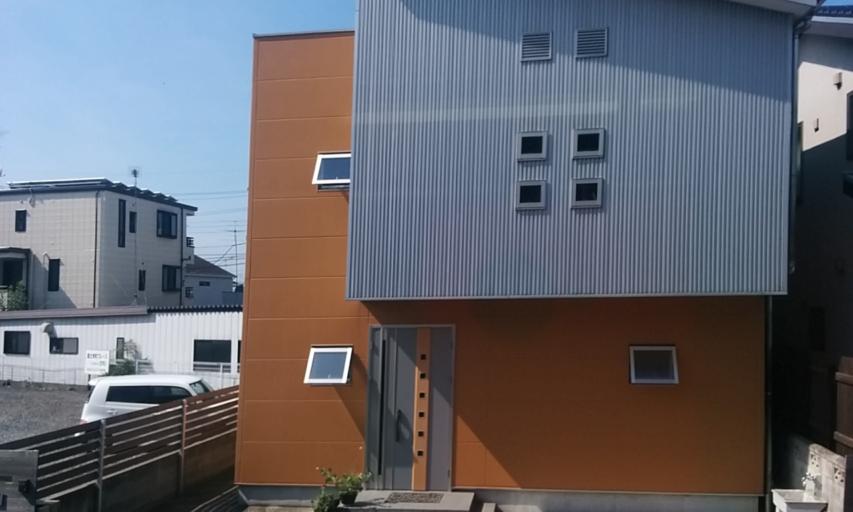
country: JP
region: Saitama
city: Kazo
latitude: 36.1223
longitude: 139.5969
